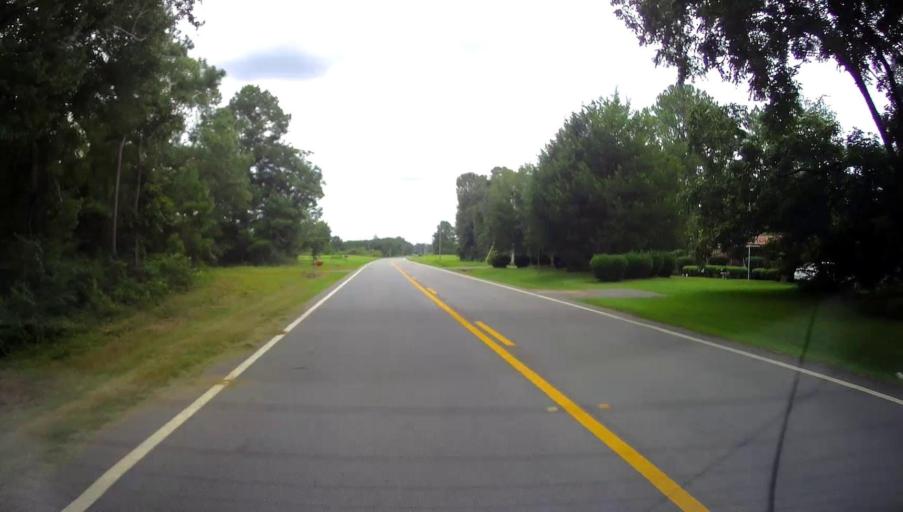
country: US
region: Georgia
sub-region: Macon County
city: Oglethorpe
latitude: 32.2732
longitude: -84.1229
